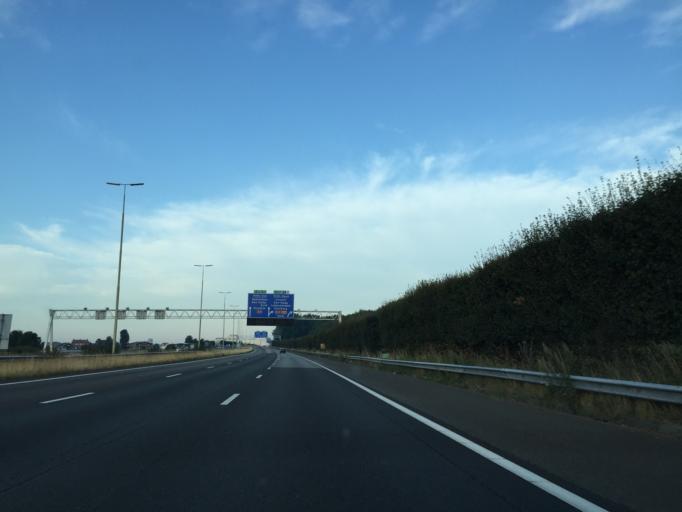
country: NL
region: South Holland
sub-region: Gemeente Leidschendam-Voorburg
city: Voorburg
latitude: 52.0830
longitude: 4.4112
